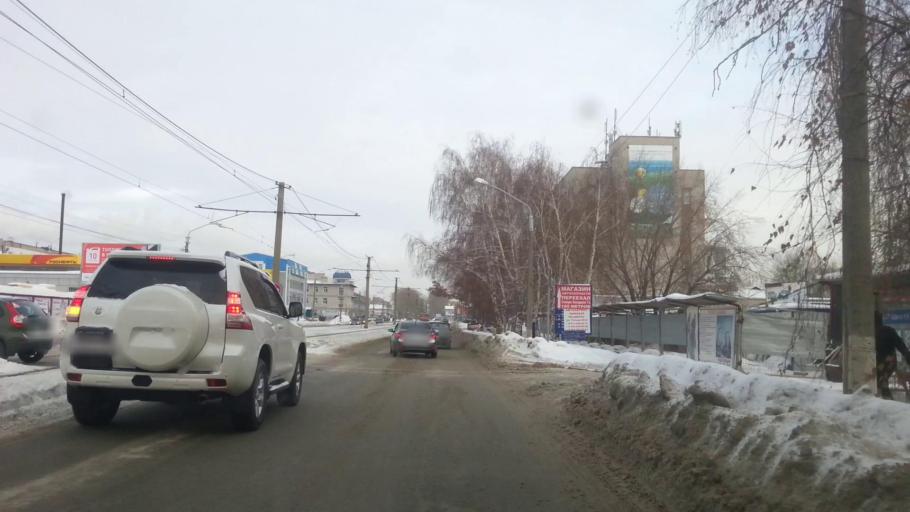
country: RU
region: Altai Krai
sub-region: Gorod Barnaulskiy
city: Barnaul
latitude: 53.3736
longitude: 83.7509
